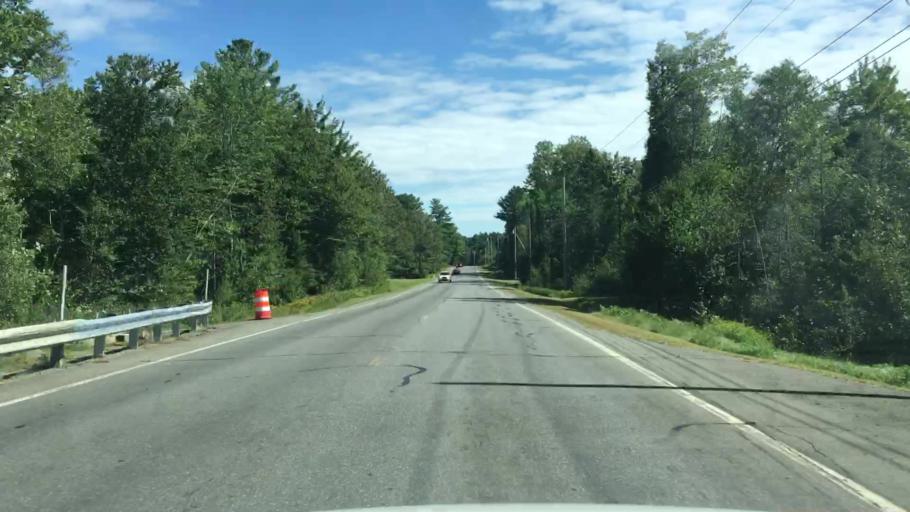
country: US
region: Maine
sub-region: Penobscot County
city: Garland
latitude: 45.0897
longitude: -69.2195
